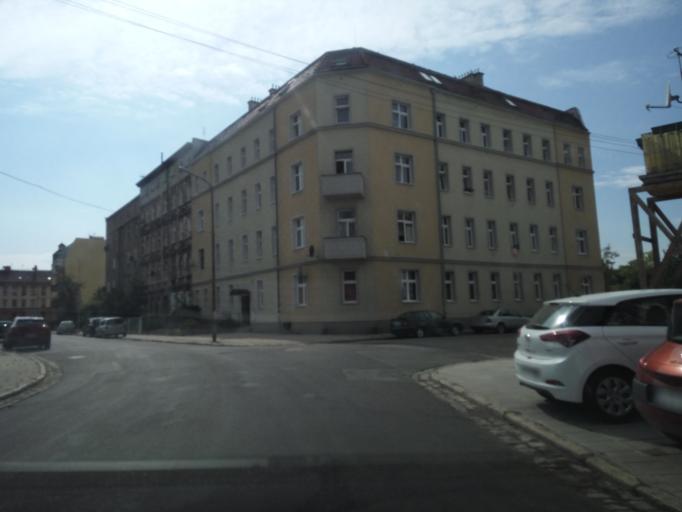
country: PL
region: Lower Silesian Voivodeship
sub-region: Powiat wroclawski
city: Radwanice
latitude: 51.0617
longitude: 17.0843
